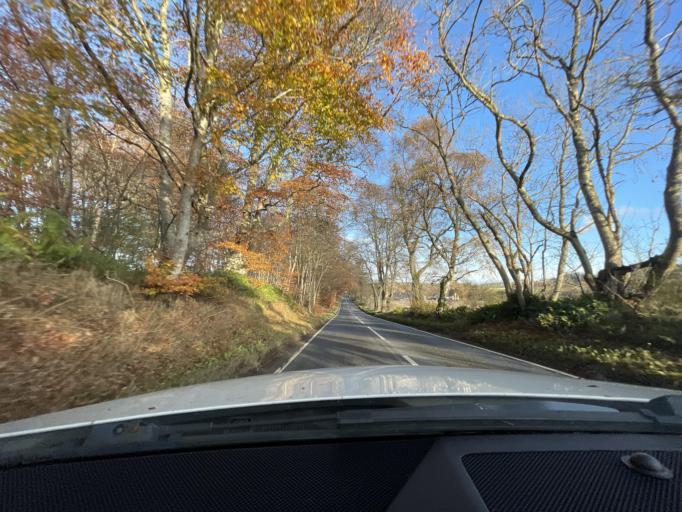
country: GB
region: Scotland
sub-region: Highland
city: Inverness
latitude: 57.4270
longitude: -4.2864
